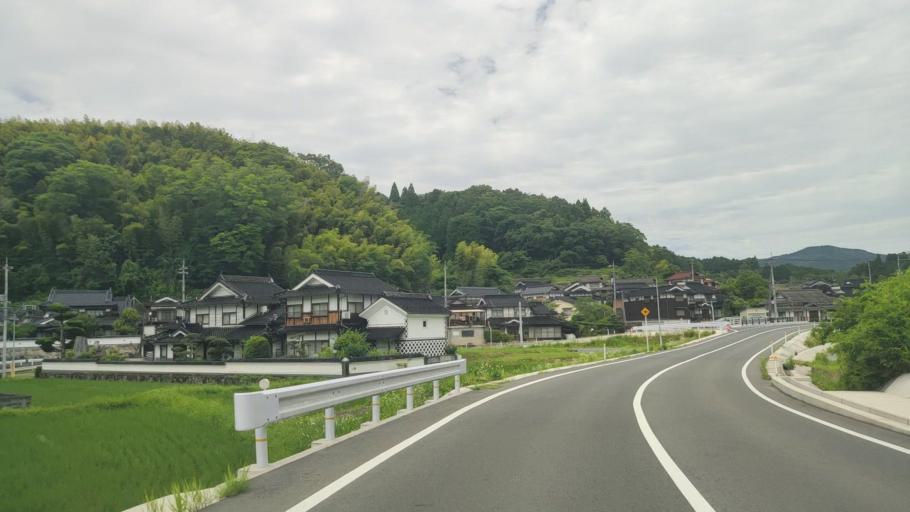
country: JP
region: Okayama
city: Tsuyama
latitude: 35.0682
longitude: 134.2356
